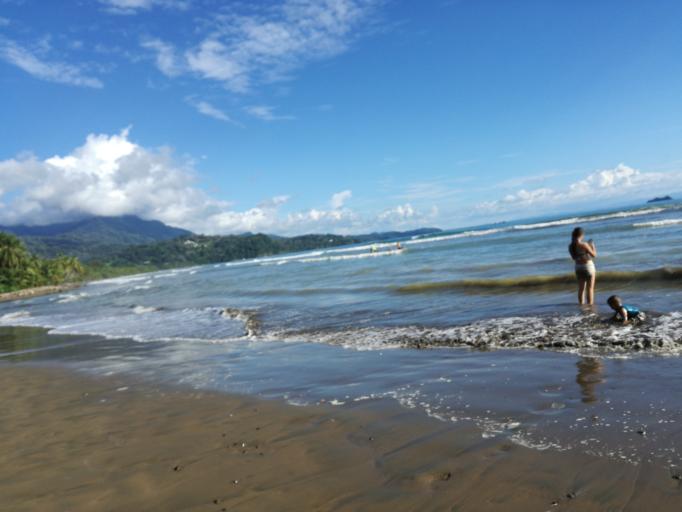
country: CR
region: San Jose
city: Daniel Flores
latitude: 9.1539
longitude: -83.7498
